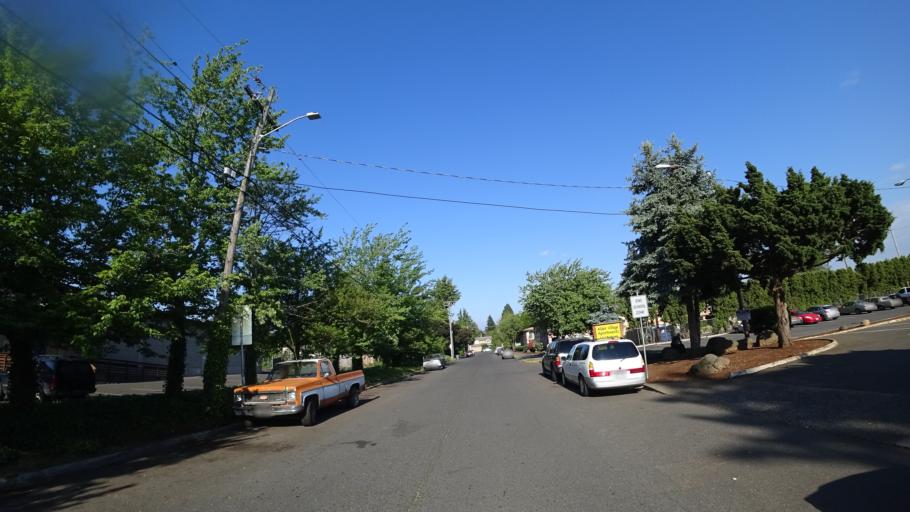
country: US
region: Oregon
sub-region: Multnomah County
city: Fairview
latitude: 45.5173
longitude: -122.4987
